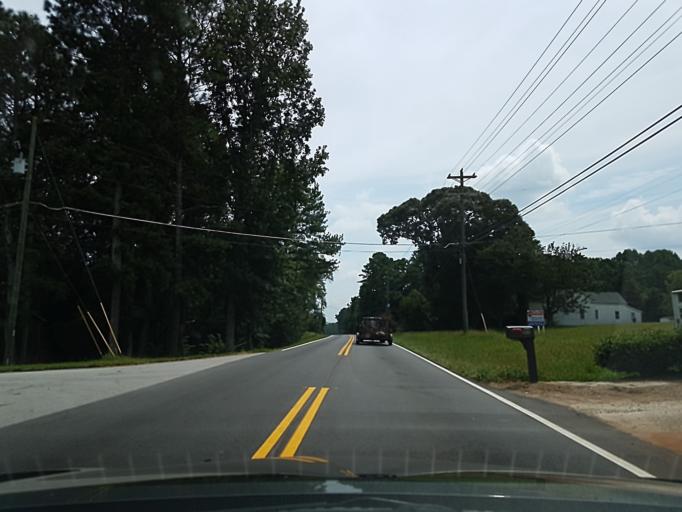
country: US
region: Georgia
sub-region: Douglas County
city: Douglasville
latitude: 33.6925
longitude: -84.7160
